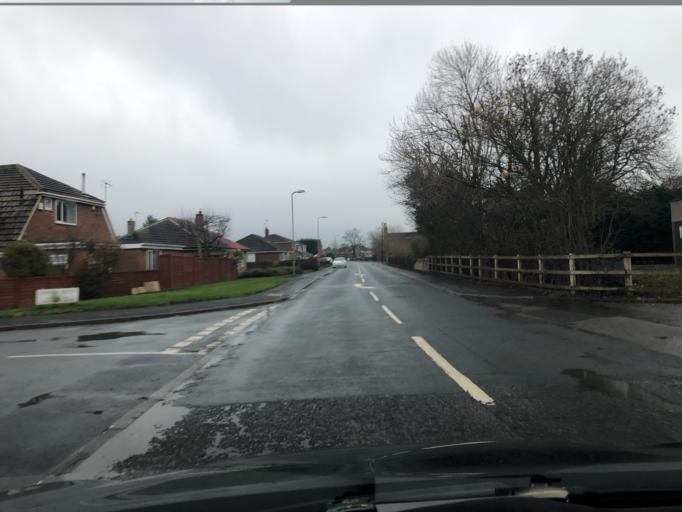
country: GB
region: England
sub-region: North Yorkshire
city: Stokesley
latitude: 54.4770
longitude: -1.1874
